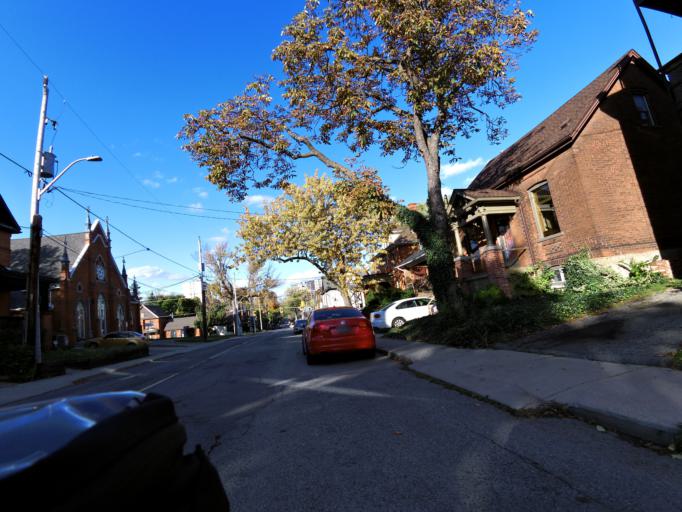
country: CA
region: Ontario
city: Hamilton
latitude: 43.2511
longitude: -79.8807
